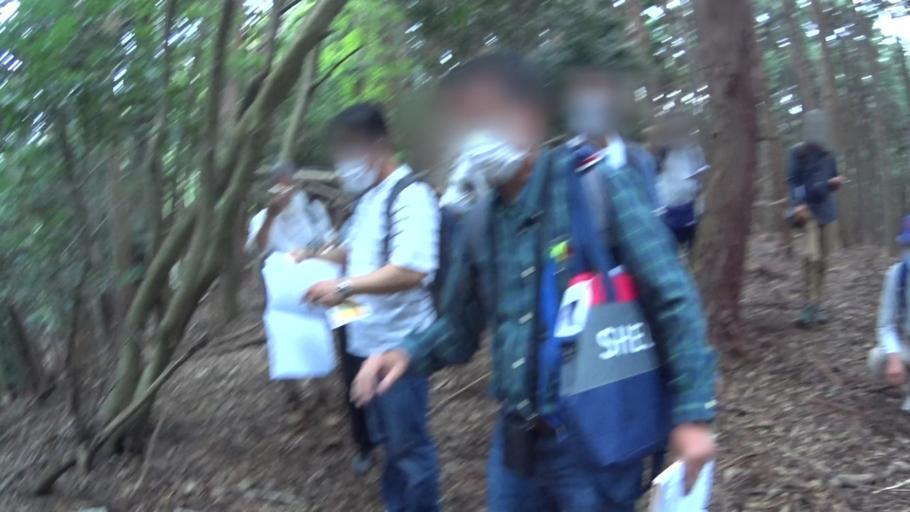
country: JP
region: Osaka
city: Kishiwada
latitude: 34.4933
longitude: 135.3258
